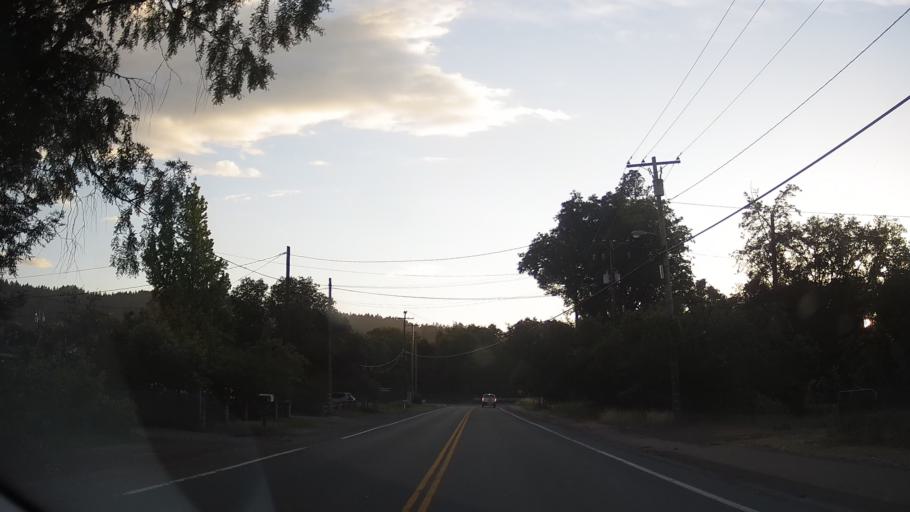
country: US
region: California
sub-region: Mendocino County
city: Willits
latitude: 39.3976
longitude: -123.3476
